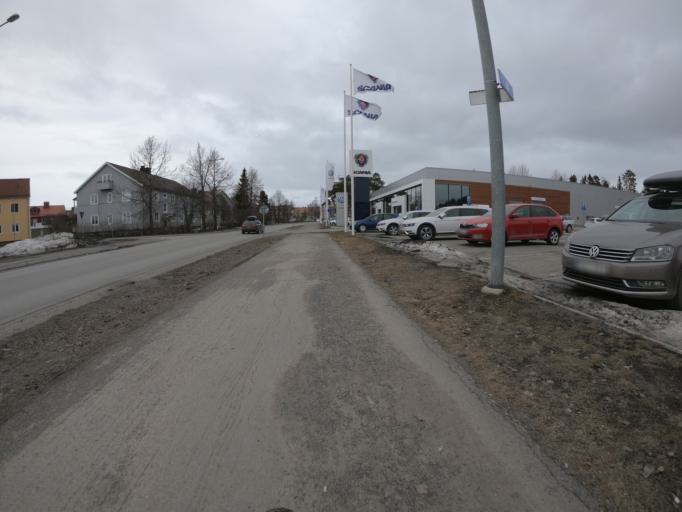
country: SE
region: Vaesterbotten
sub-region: Umea Kommun
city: Umea
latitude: 63.8336
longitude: 20.2817
